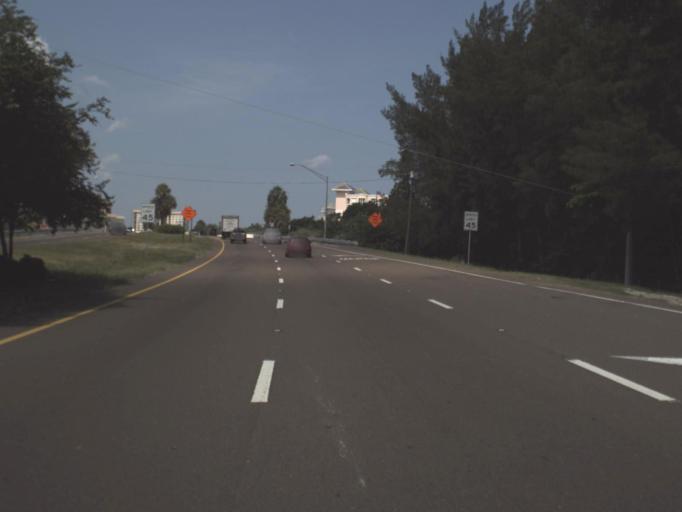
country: US
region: Florida
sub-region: Pinellas County
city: Gulfport
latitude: 27.7189
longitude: -82.6956
